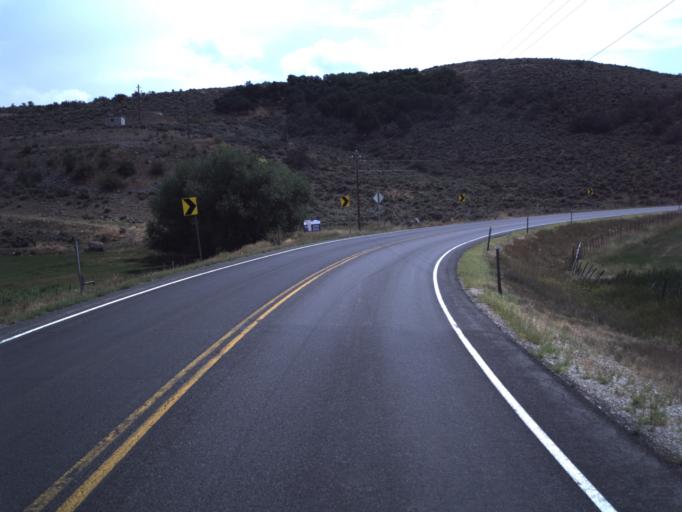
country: US
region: Utah
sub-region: Summit County
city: Francis
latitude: 40.6106
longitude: -111.2600
